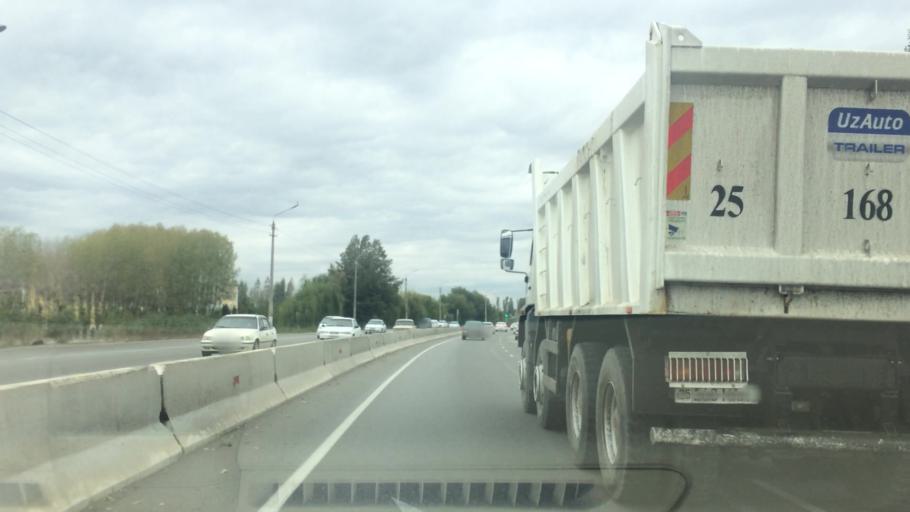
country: UZ
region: Jizzax
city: Jizzax
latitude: 39.9904
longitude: 67.5828
